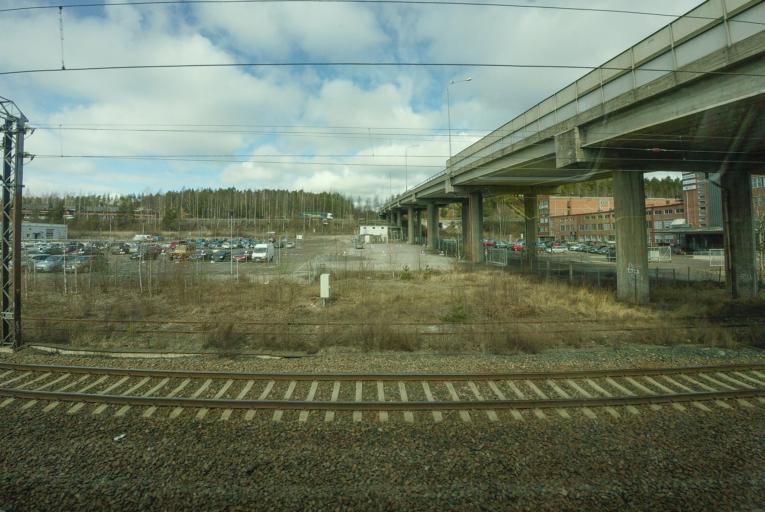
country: FI
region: Paijanne Tavastia
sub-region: Lahti
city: Lahti
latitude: 60.9755
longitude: 25.6749
